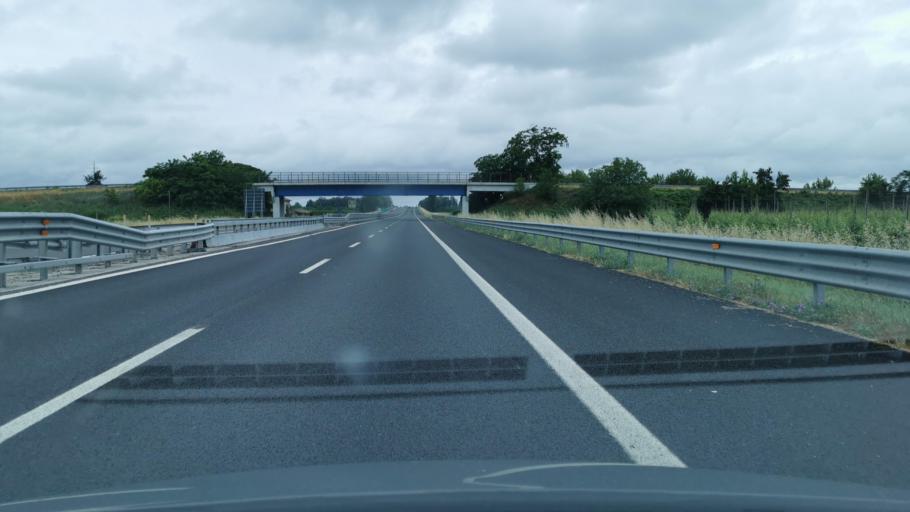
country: IT
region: Emilia-Romagna
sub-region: Provincia di Ravenna
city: Russi
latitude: 44.4040
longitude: 12.0377
